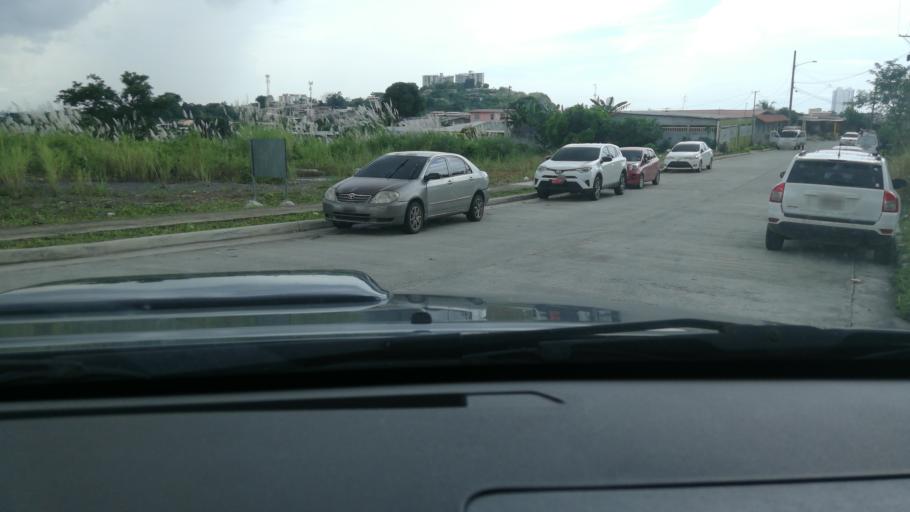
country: PA
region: Panama
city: San Miguelito
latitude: 9.0521
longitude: -79.4782
